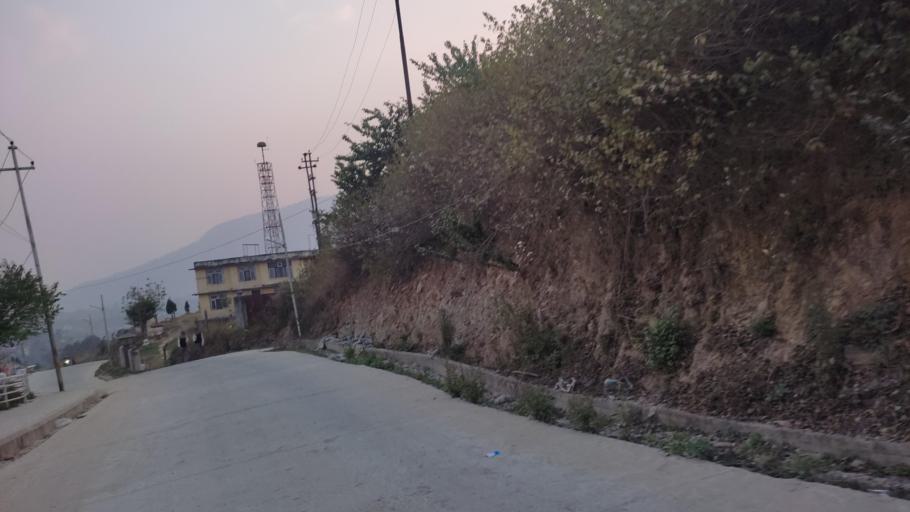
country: NP
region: Central Region
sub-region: Bagmati Zone
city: Patan
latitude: 27.6639
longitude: 85.2942
